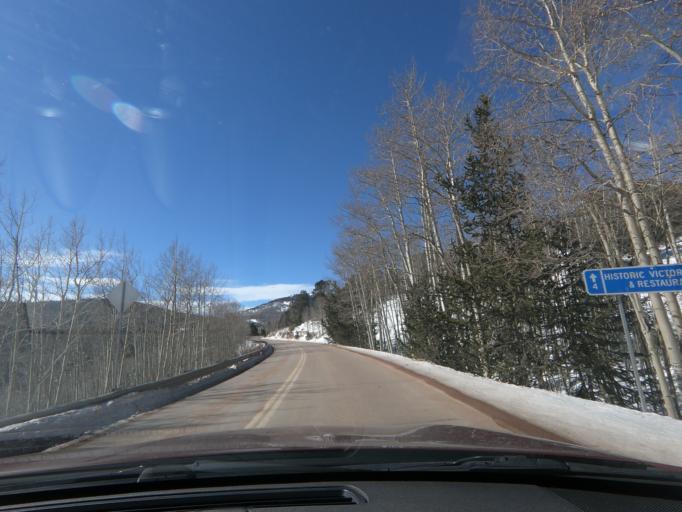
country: US
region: Colorado
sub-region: Teller County
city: Cripple Creek
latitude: 38.7440
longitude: -105.1013
